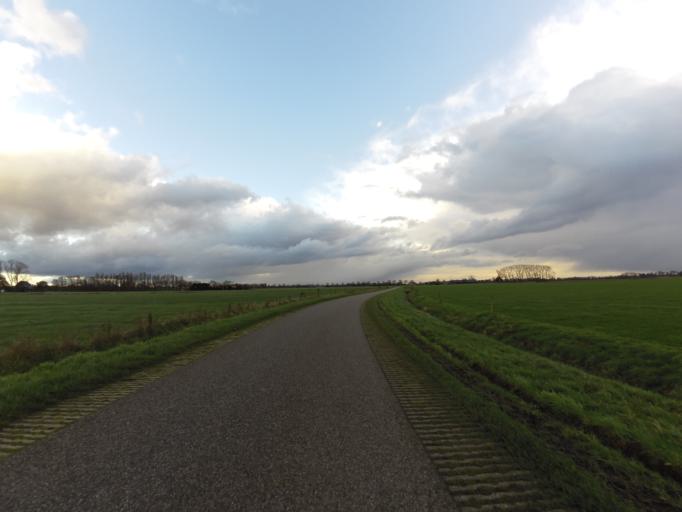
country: NL
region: Gelderland
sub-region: Oude IJsselstreek
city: Gendringen
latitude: 51.8512
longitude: 6.3577
